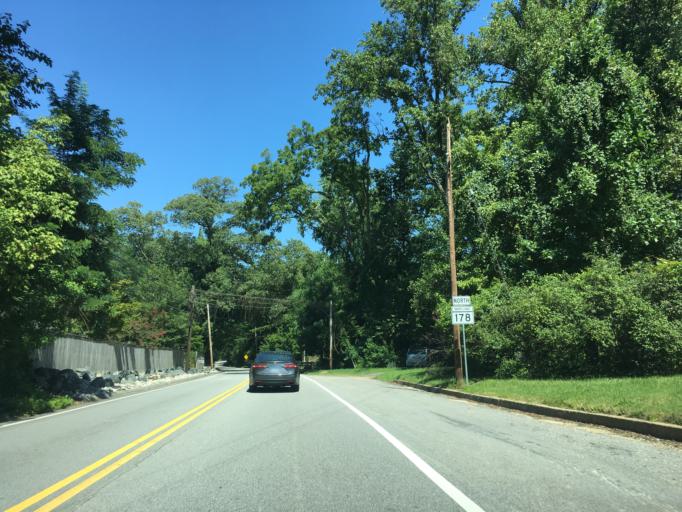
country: US
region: Maryland
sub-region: Anne Arundel County
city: Crownsville
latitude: 39.0421
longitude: -76.6065
